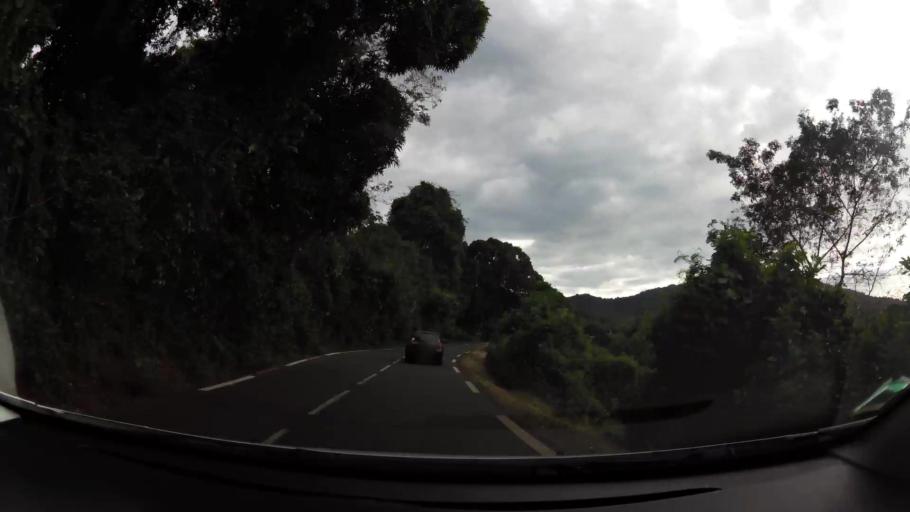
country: YT
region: Dembeni
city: Dembeni
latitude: -12.8406
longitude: 45.1661
